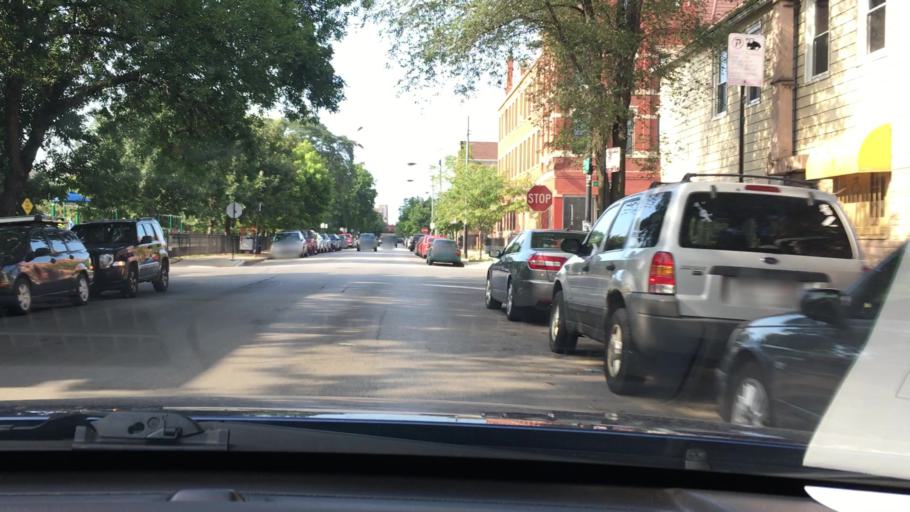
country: US
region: Illinois
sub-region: Cook County
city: Chicago
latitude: 41.8557
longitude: -87.6709
